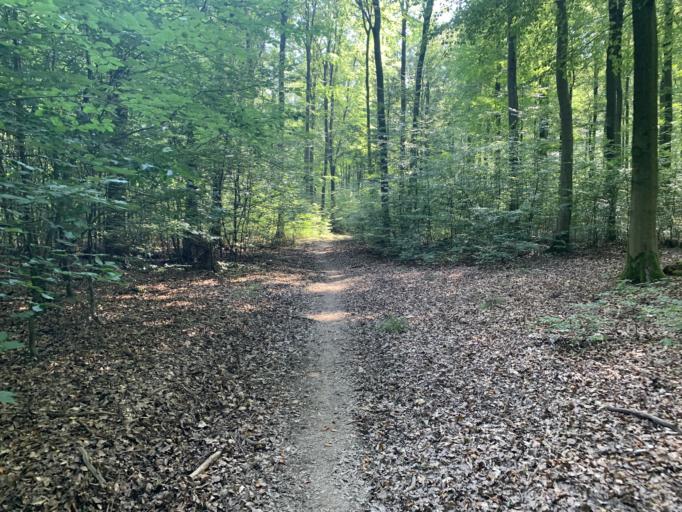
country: DE
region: Rheinland-Pfalz
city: Rettert
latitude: 50.2153
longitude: 7.9404
